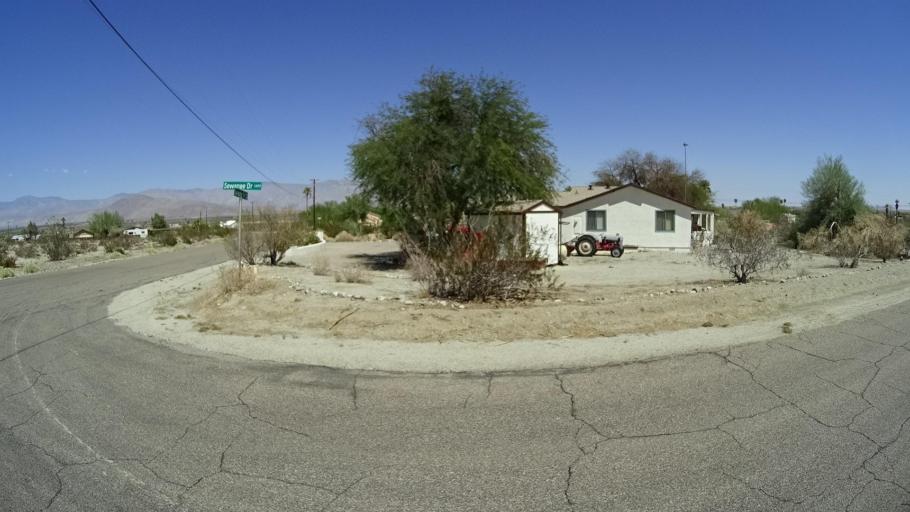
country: US
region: California
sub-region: San Diego County
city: Borrego Springs
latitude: 33.2076
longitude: -116.3398
